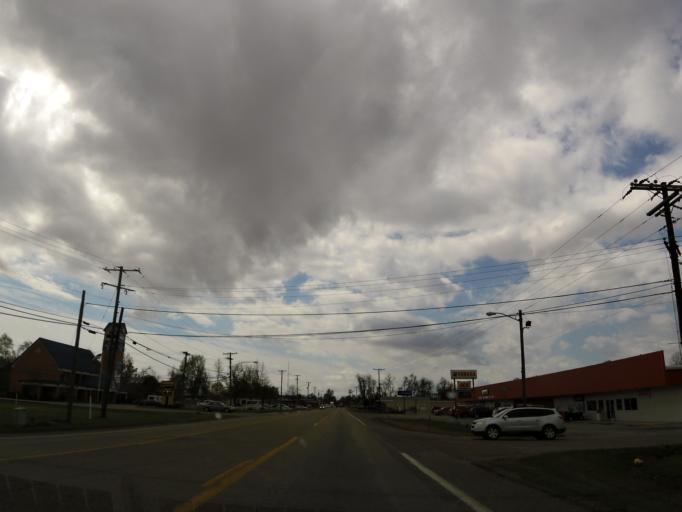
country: US
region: Arkansas
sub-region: Clay County
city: Corning
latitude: 36.4189
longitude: -90.5863
